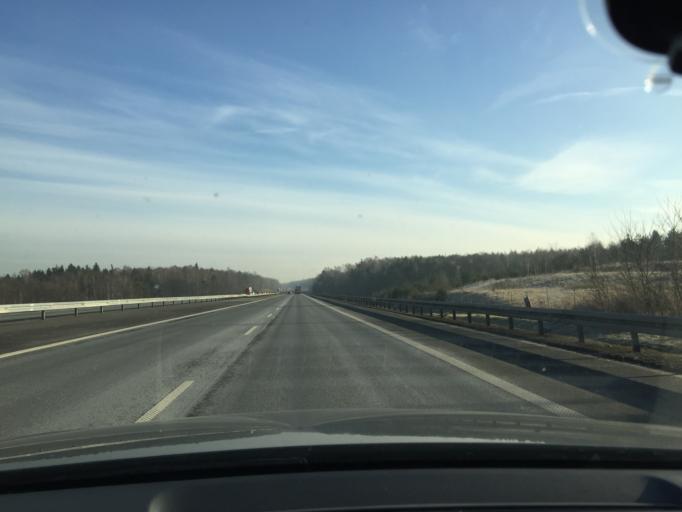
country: PL
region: Silesian Voivodeship
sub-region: Katowice
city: Murcki
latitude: 50.2268
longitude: 19.0798
